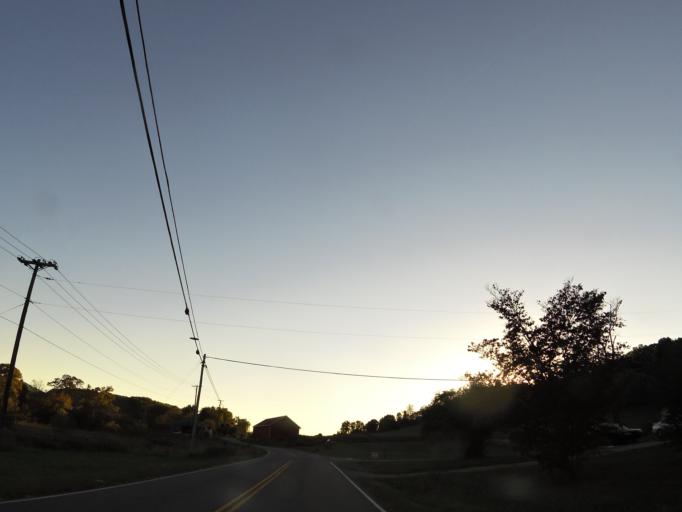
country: US
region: Tennessee
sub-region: Union County
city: Luttrell
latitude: 36.2649
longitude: -83.6494
